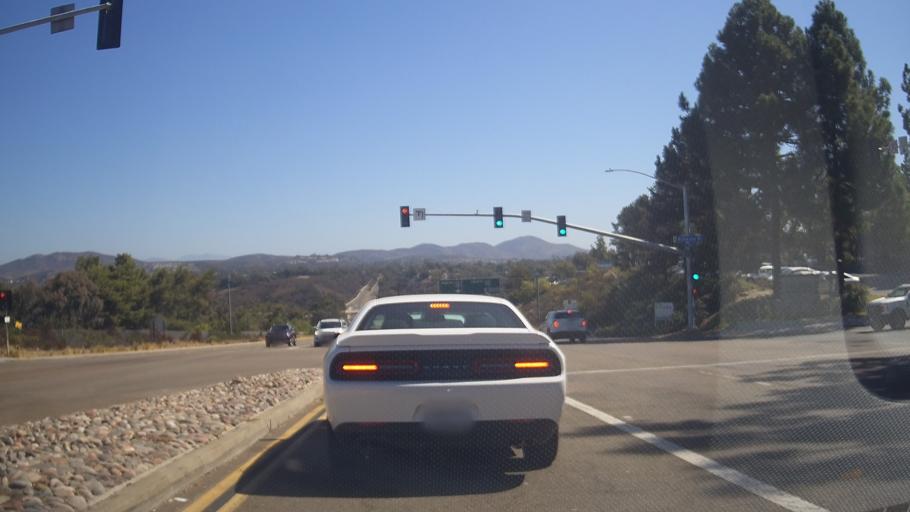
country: US
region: California
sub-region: San Diego County
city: San Diego
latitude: 32.8221
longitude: -117.1253
